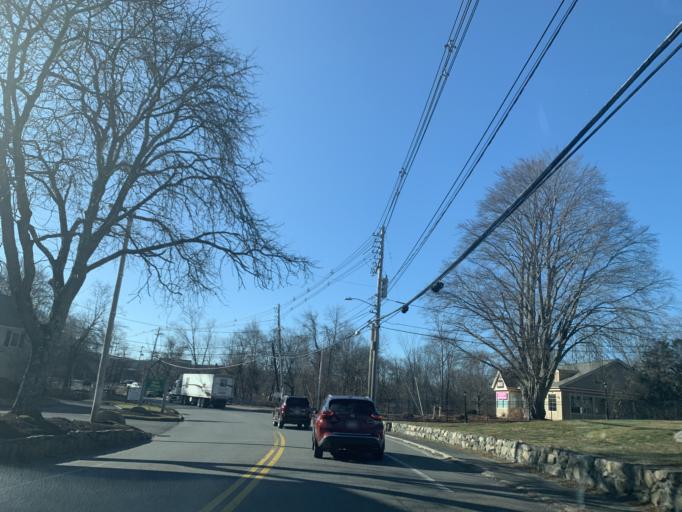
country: US
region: Massachusetts
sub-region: Middlesex County
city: Sudbury
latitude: 42.3622
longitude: -71.4168
